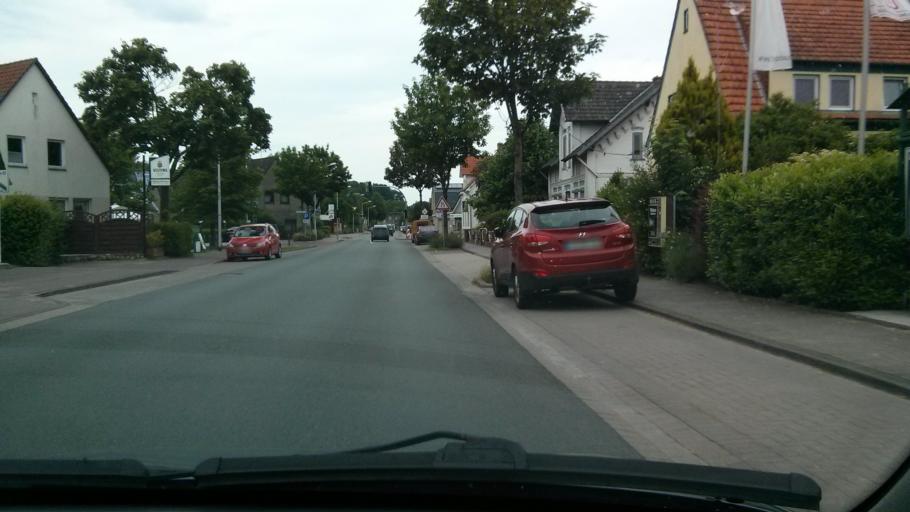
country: DE
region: Lower Saxony
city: Loxstedt
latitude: 53.4714
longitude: 8.6510
